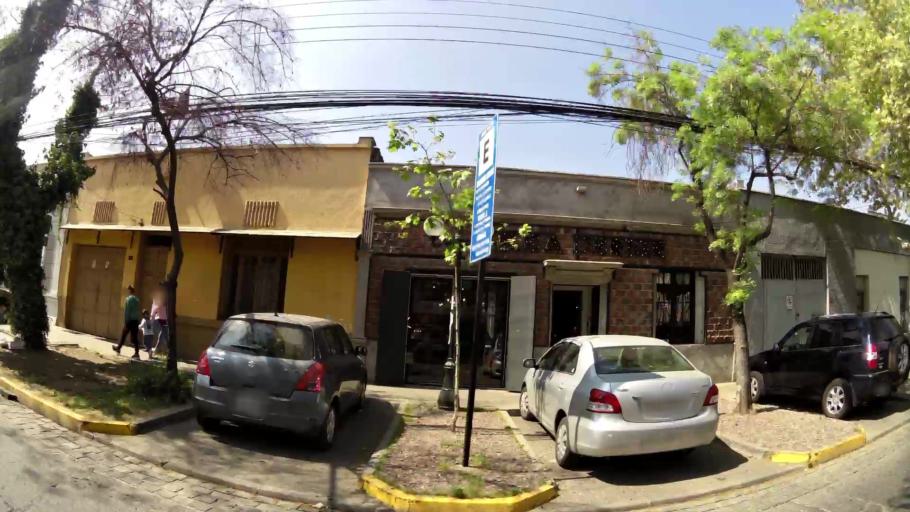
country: CL
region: Santiago Metropolitan
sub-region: Provincia de Santiago
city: Santiago
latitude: -33.4476
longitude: -70.6248
